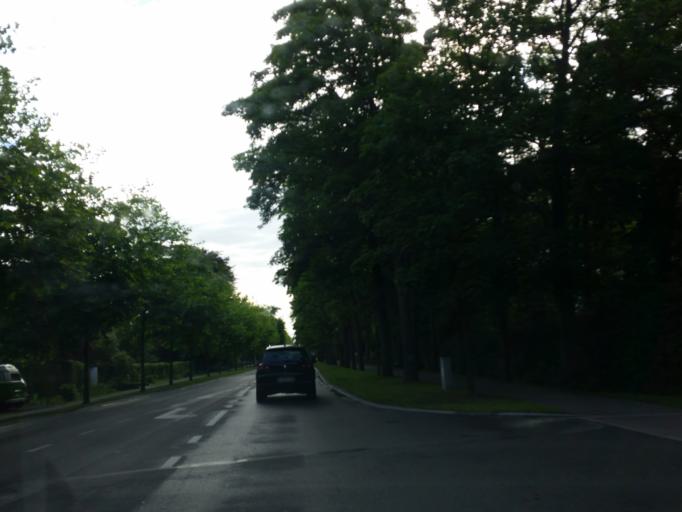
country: BE
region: Flanders
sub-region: Provincie Antwerpen
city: Brasschaat
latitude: 51.2910
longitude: 4.5022
